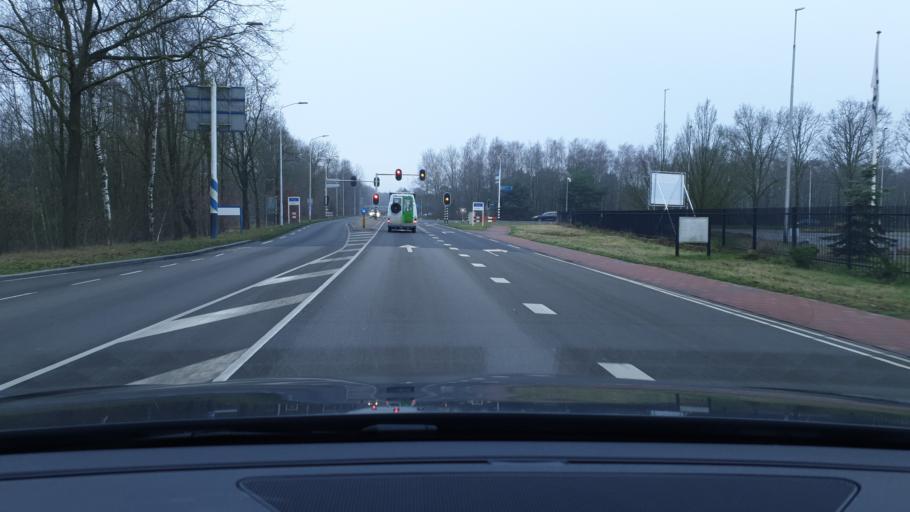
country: NL
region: North Brabant
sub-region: Gemeente Best
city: Best
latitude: 51.4887
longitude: 5.3901
